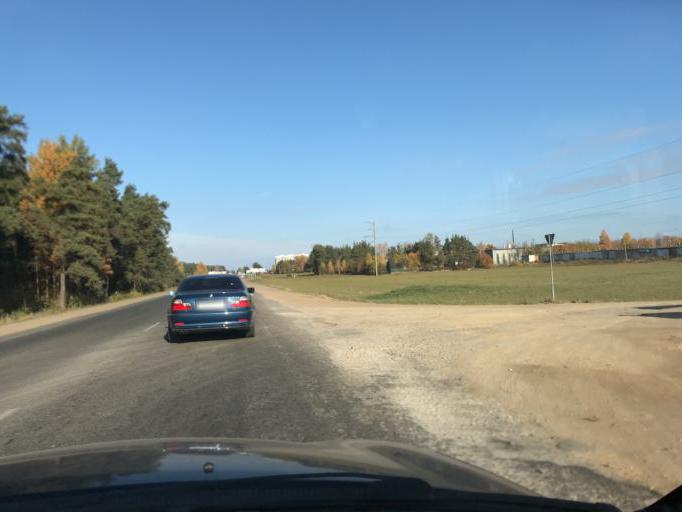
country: BY
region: Grodnenskaya
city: Lida
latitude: 53.8846
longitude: 25.2549
